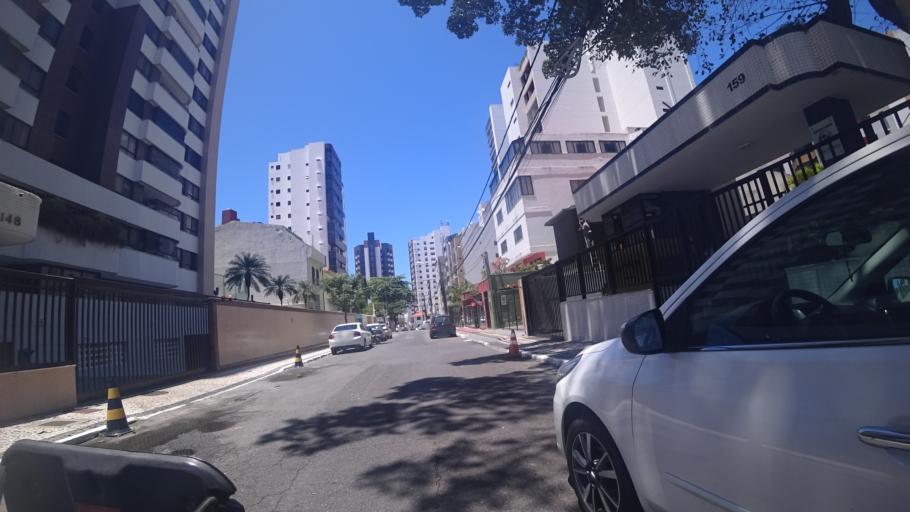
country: BR
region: Bahia
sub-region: Salvador
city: Salvador
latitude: -12.9868
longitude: -38.4617
